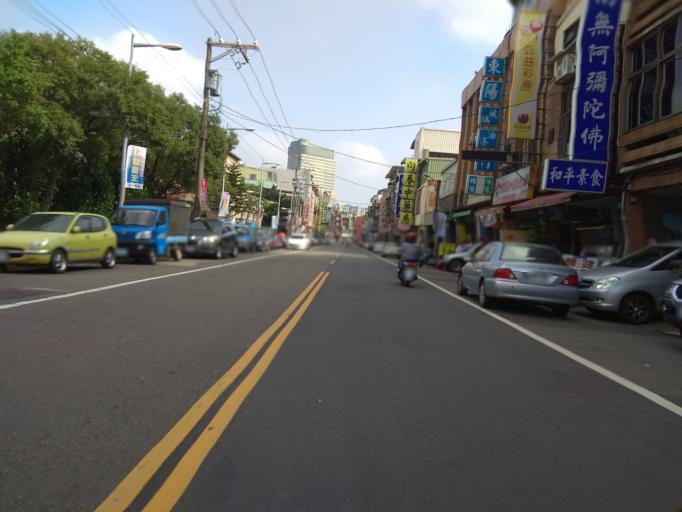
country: TW
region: Taiwan
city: Taoyuan City
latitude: 24.9535
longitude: 121.2160
